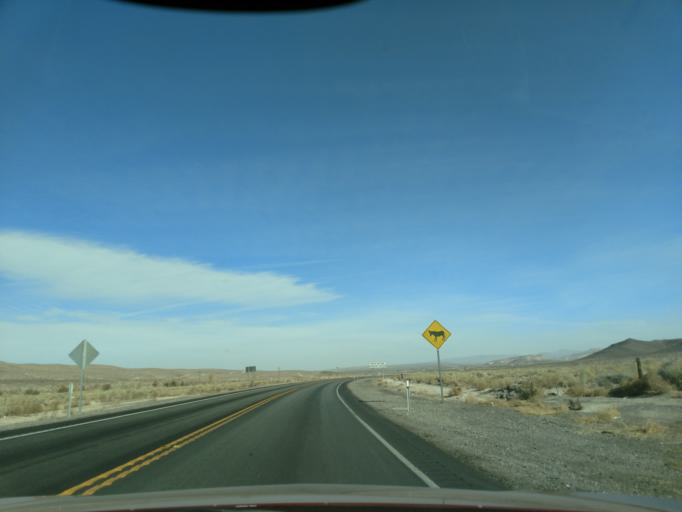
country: US
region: Nevada
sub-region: Nye County
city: Beatty
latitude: 36.9178
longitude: -116.7503
